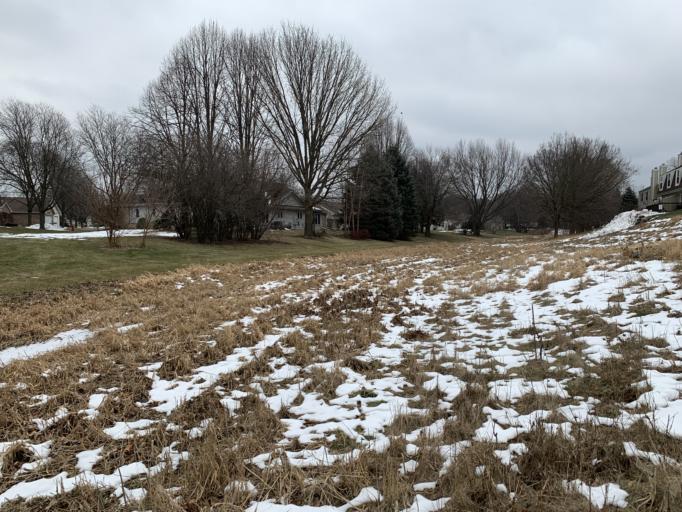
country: US
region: Wisconsin
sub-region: Dane County
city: Middleton
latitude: 43.0767
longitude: -89.5110
